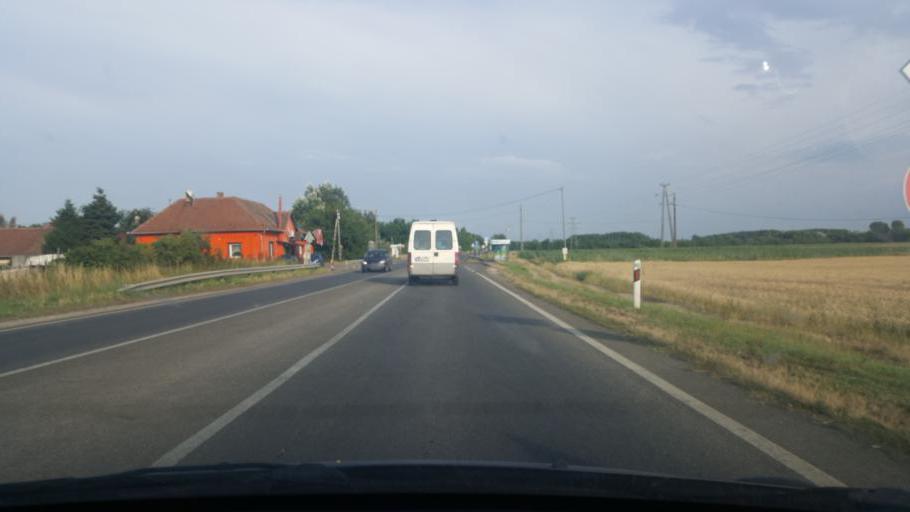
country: HU
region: Pest
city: Ullo
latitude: 47.3643
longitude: 19.3839
